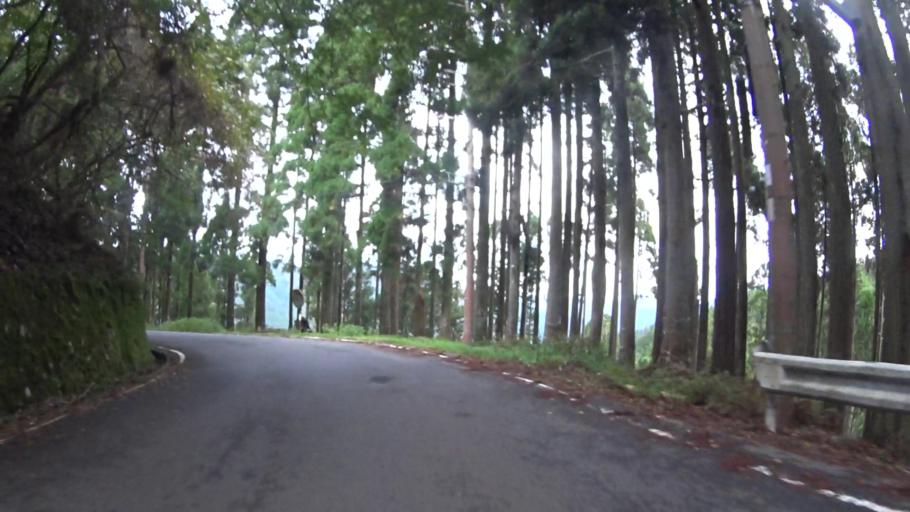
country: JP
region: Shiga Prefecture
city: Kitahama
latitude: 35.1593
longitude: 135.7850
